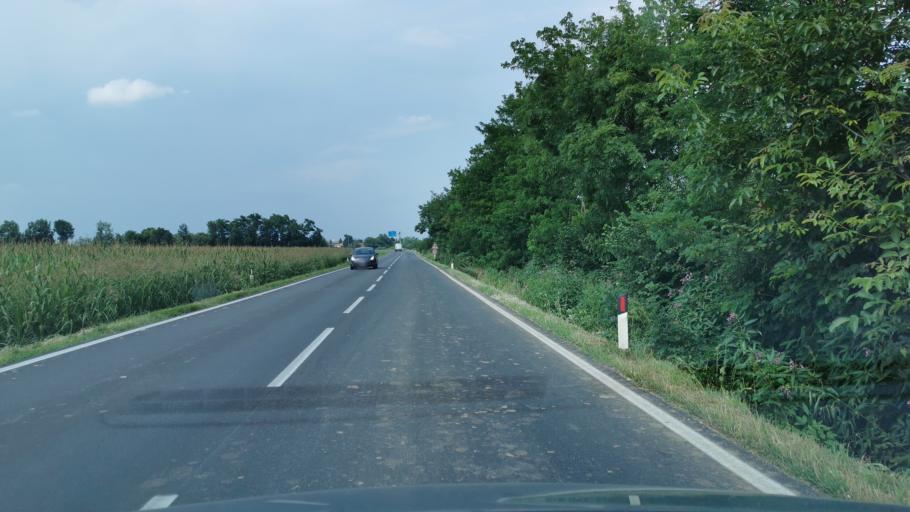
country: IT
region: Piedmont
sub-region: Provincia di Cuneo
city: Tarantasca
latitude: 44.4802
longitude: 7.5435
